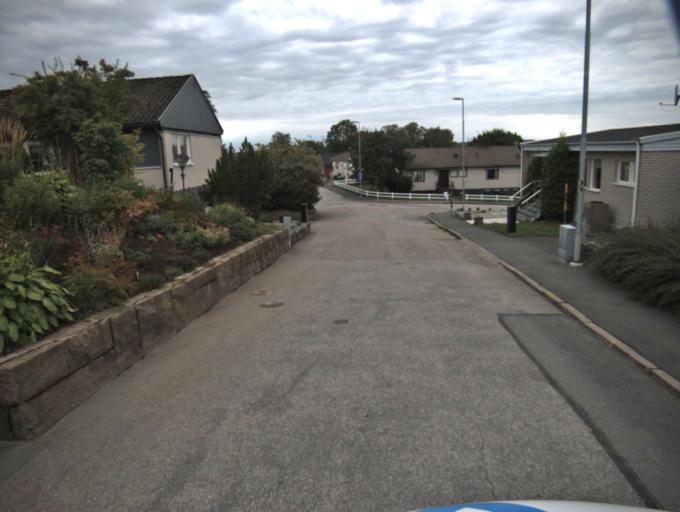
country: SE
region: Vaestra Goetaland
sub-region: Ulricehamns Kommun
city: Ulricehamn
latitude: 57.7987
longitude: 13.4293
